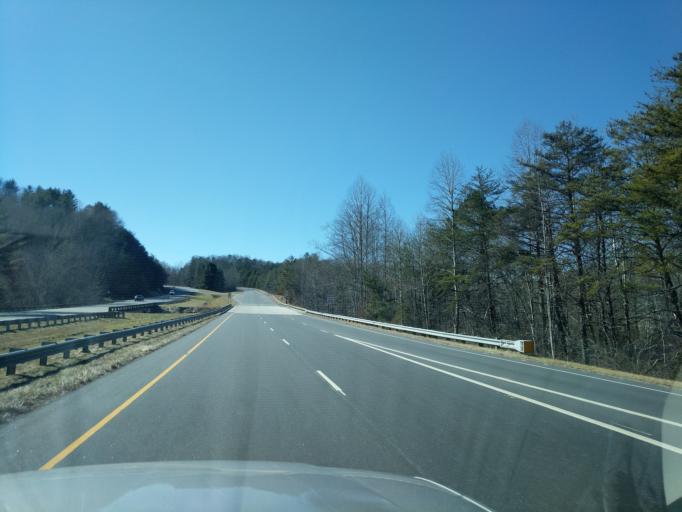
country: US
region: North Carolina
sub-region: Swain County
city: Bryson City
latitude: 35.3927
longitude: -83.4770
